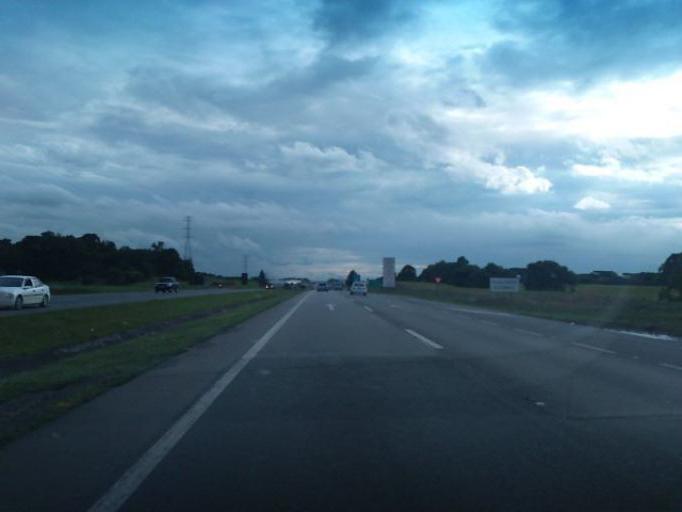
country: BR
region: Parana
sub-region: Piraquara
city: Piraquara
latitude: -25.4940
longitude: -49.1152
